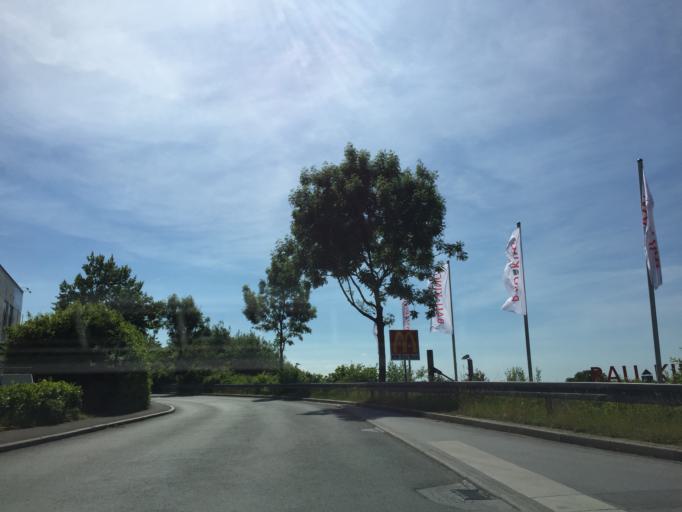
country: DE
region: North Rhine-Westphalia
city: Iserlohn
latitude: 51.3863
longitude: 7.7267
